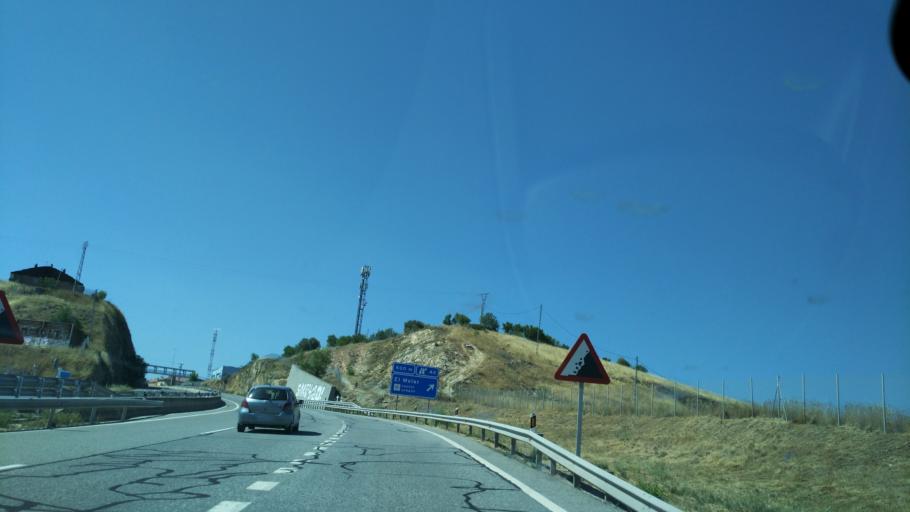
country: ES
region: Madrid
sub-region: Provincia de Madrid
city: El Molar
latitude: 40.7266
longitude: -3.5789
